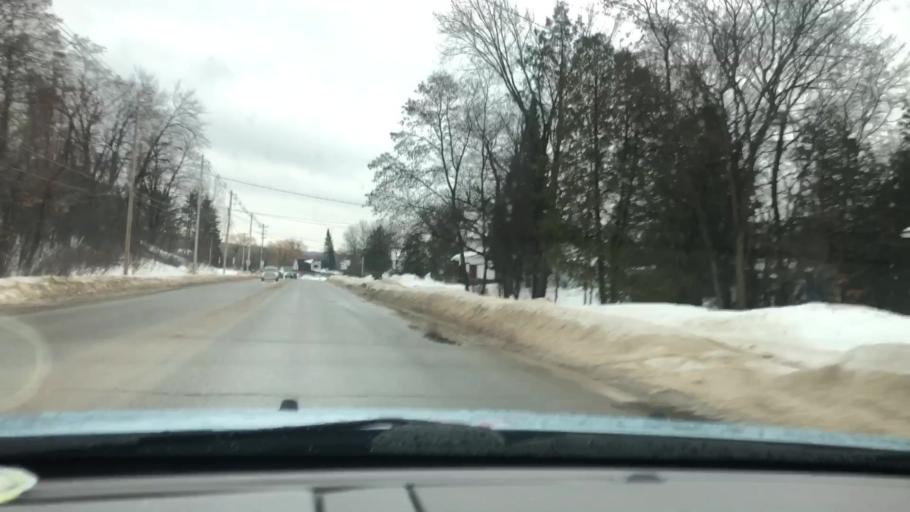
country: US
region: Michigan
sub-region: Charlevoix County
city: East Jordan
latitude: 45.1531
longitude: -85.1215
